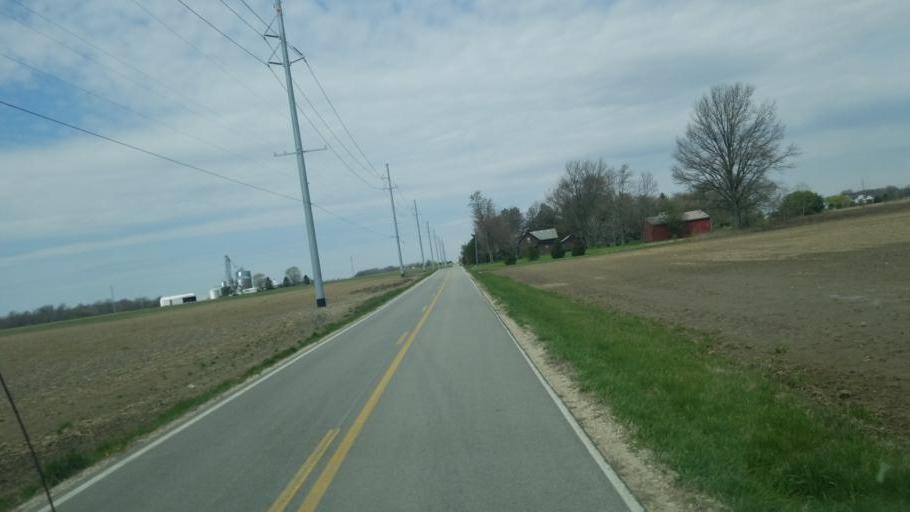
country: US
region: Ohio
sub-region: Delaware County
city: Delaware
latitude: 40.3654
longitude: -83.0943
